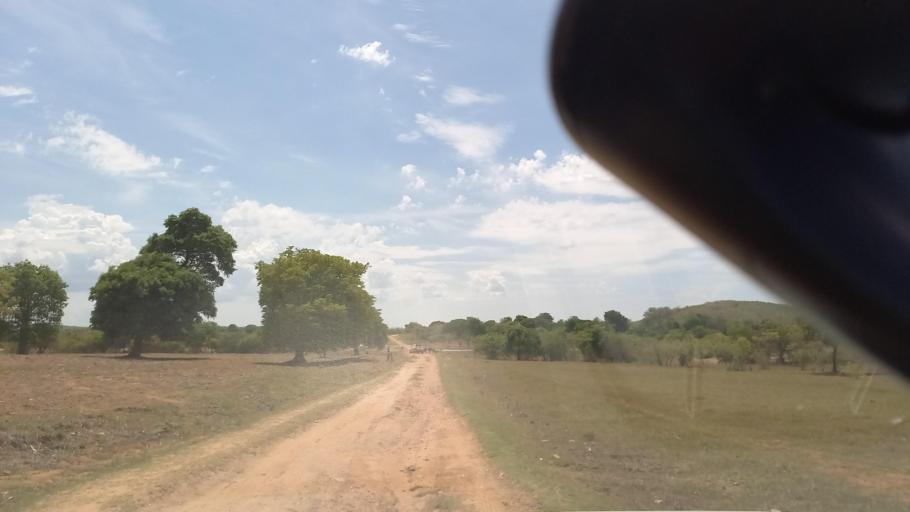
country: ZM
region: Southern
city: Mazabuka
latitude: -16.1386
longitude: 27.7587
